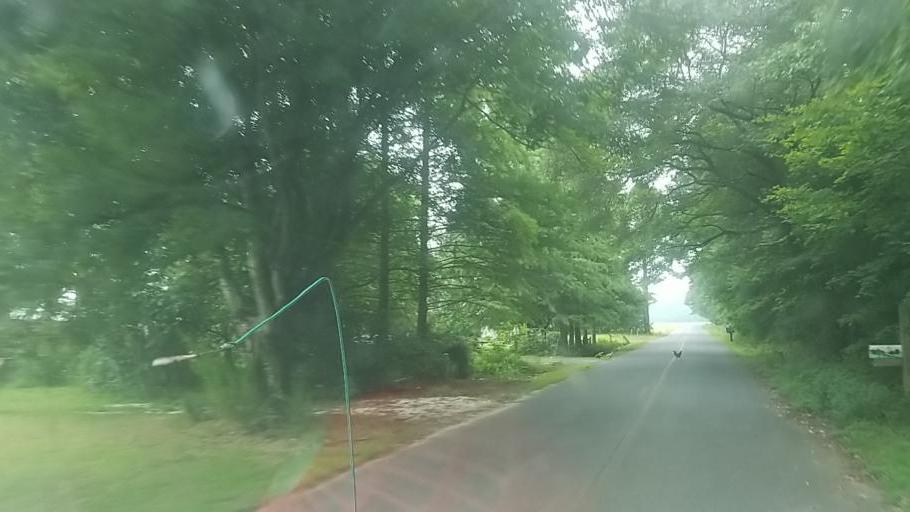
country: US
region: Delaware
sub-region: Sussex County
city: Selbyville
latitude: 38.4286
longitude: -75.2880
